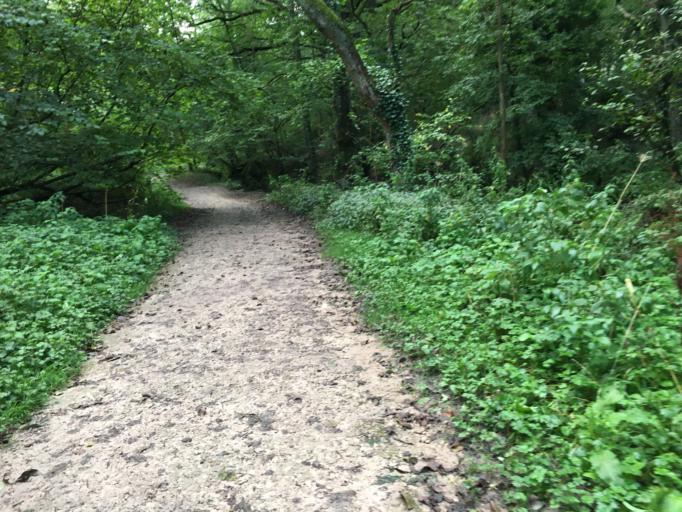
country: GB
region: England
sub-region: North Yorkshire
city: Sleights
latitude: 54.4060
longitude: -0.7308
